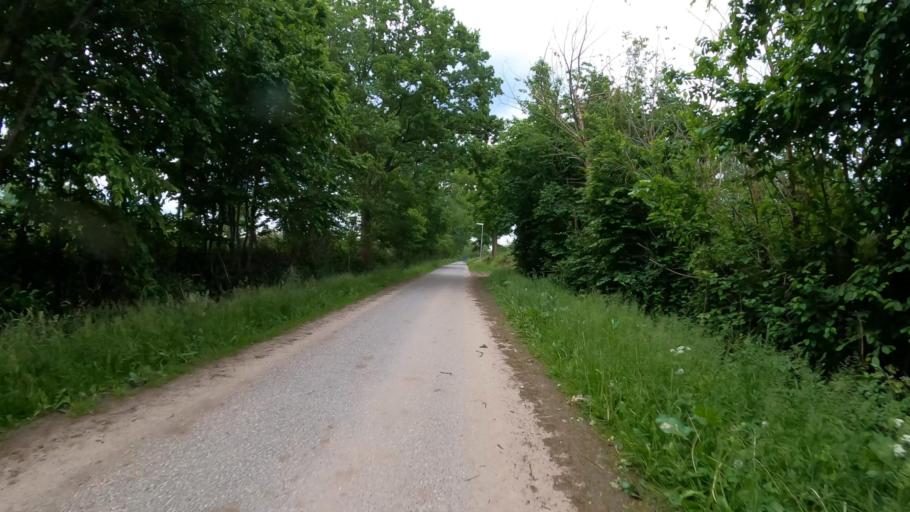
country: DE
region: Schleswig-Holstein
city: Appen
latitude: 53.6560
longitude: 9.7589
